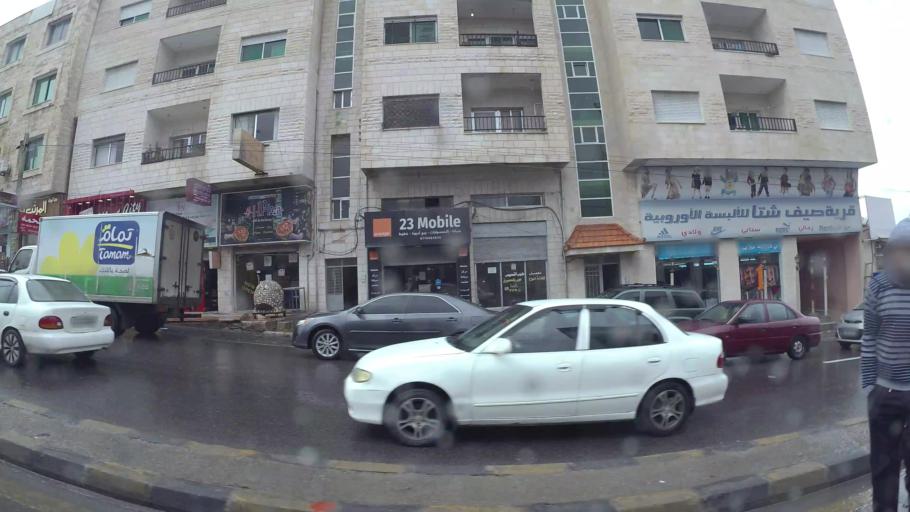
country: JO
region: Amman
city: Wadi as Sir
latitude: 32.0047
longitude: 35.7853
